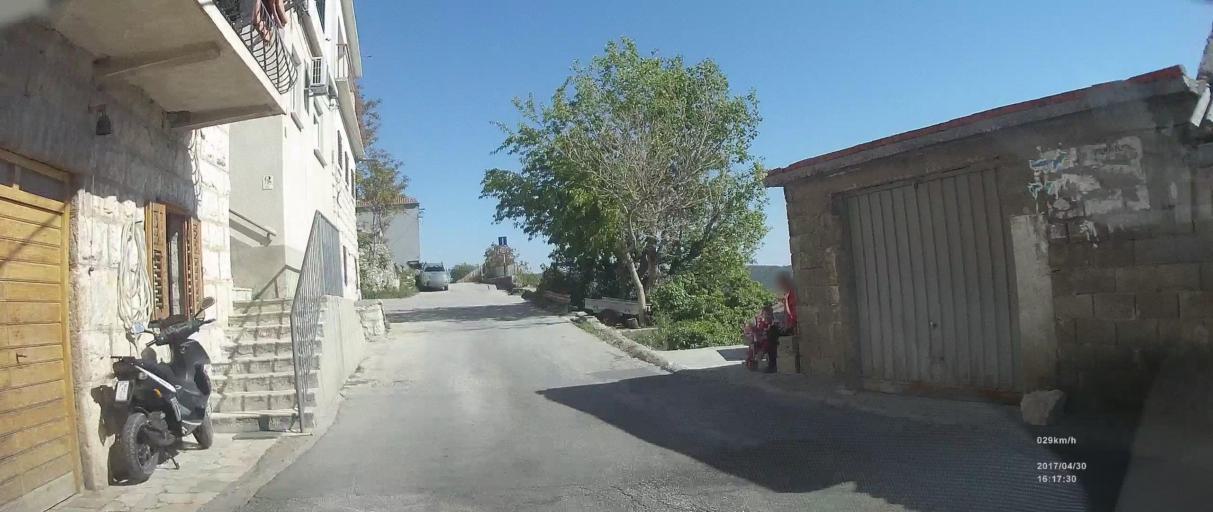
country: HR
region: Splitsko-Dalmatinska
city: Srinjine
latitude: 43.4987
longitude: 16.6105
